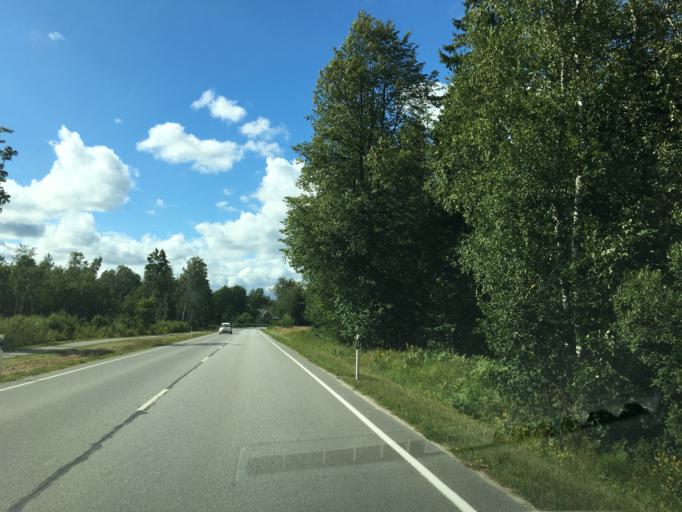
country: EE
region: Paernumaa
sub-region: Vaendra vald (alev)
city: Vandra
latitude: 58.6540
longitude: 25.0566
